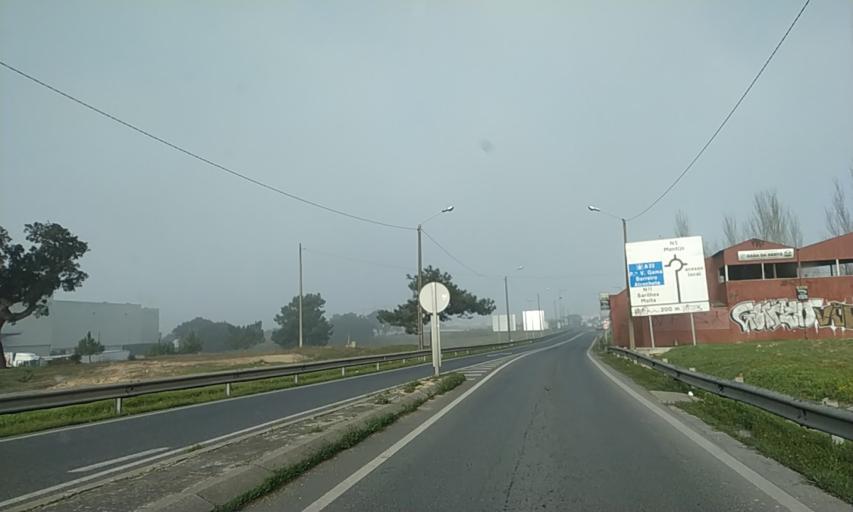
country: PT
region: Setubal
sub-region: Montijo
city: Montijo
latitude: 38.6844
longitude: -8.9424
